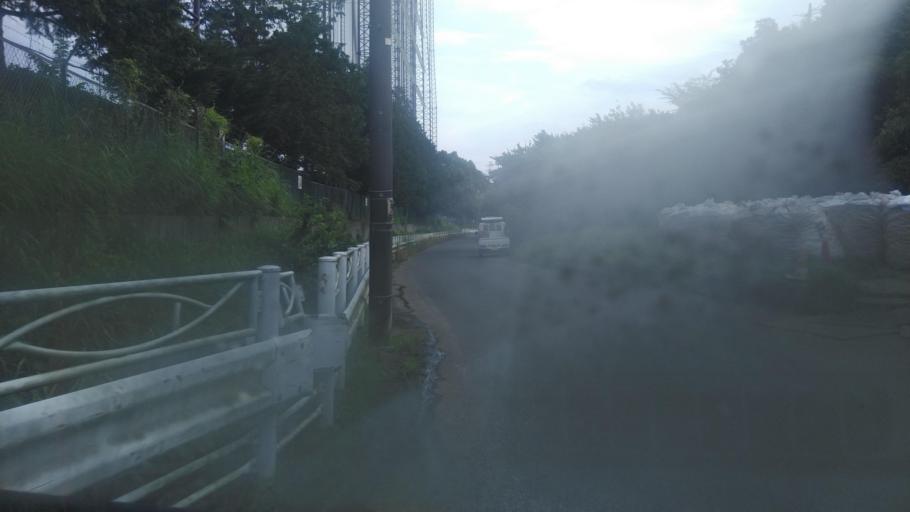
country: JP
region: Kanagawa
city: Fujisawa
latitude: 35.3930
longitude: 139.4365
